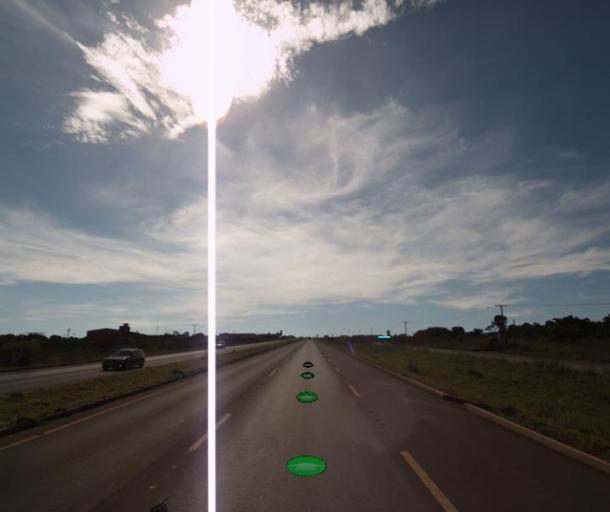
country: BR
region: Federal District
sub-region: Brasilia
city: Brasilia
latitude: -15.7397
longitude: -48.3058
